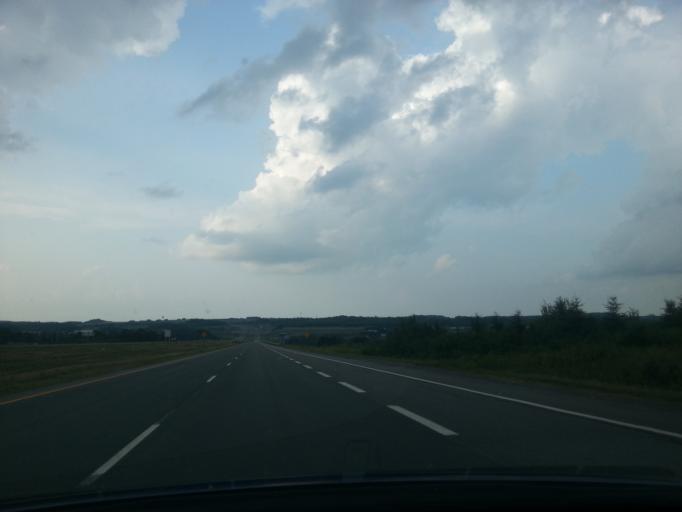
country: US
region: Maine
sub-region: Aroostook County
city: Limestone
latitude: 47.0518
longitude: -67.7647
